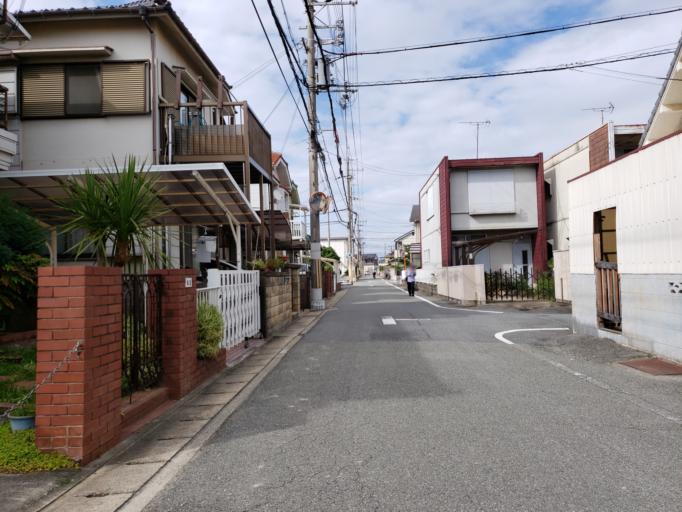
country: JP
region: Hyogo
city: Kakogawacho-honmachi
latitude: 34.7555
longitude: 134.8174
